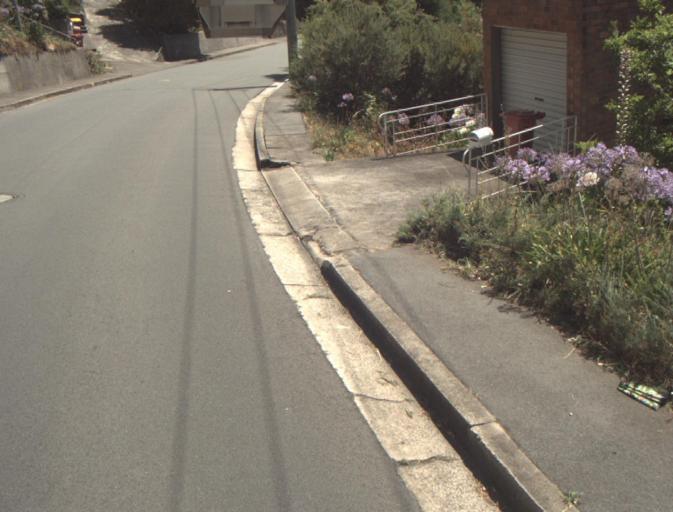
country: AU
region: Tasmania
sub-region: Launceston
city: West Launceston
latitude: -41.4570
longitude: 147.1318
